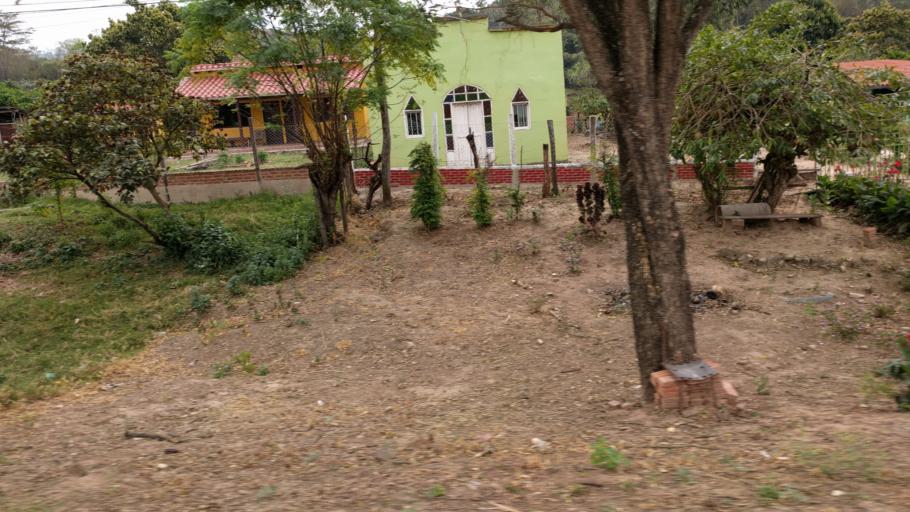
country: BO
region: Santa Cruz
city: Jorochito
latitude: -18.1322
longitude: -63.4711
